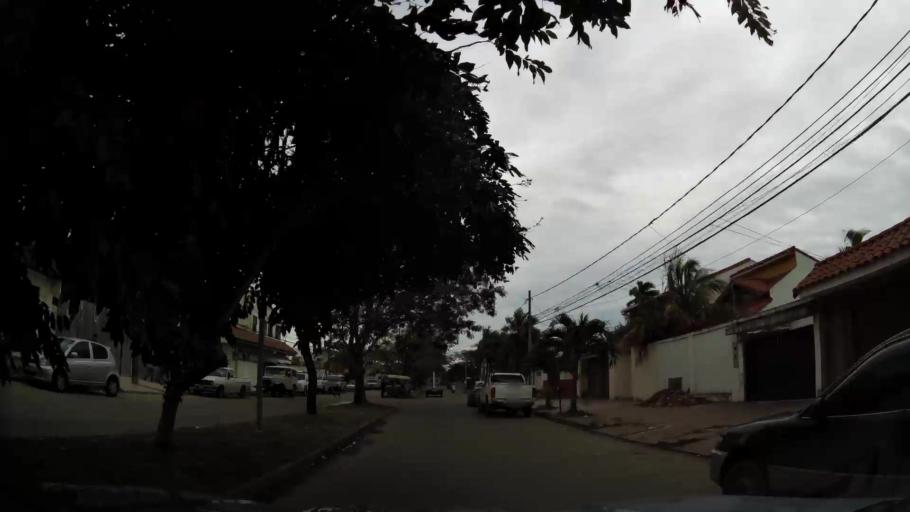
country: BO
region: Santa Cruz
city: Santa Cruz de la Sierra
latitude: -17.7783
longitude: -63.1594
